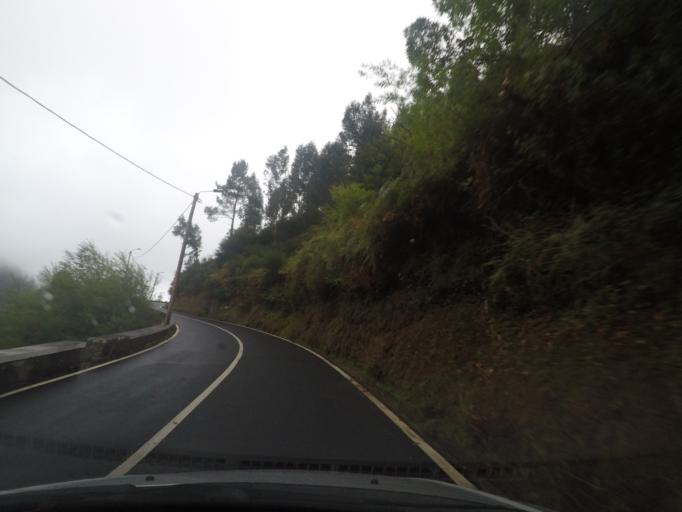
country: PT
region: Madeira
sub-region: Santa Cruz
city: Camacha
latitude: 32.7042
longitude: -16.8426
